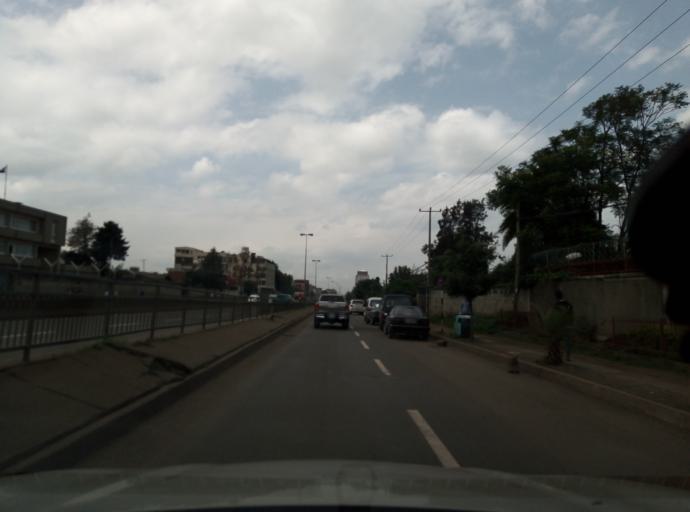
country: ET
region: Adis Abeba
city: Addis Ababa
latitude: 9.0052
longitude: 38.7186
